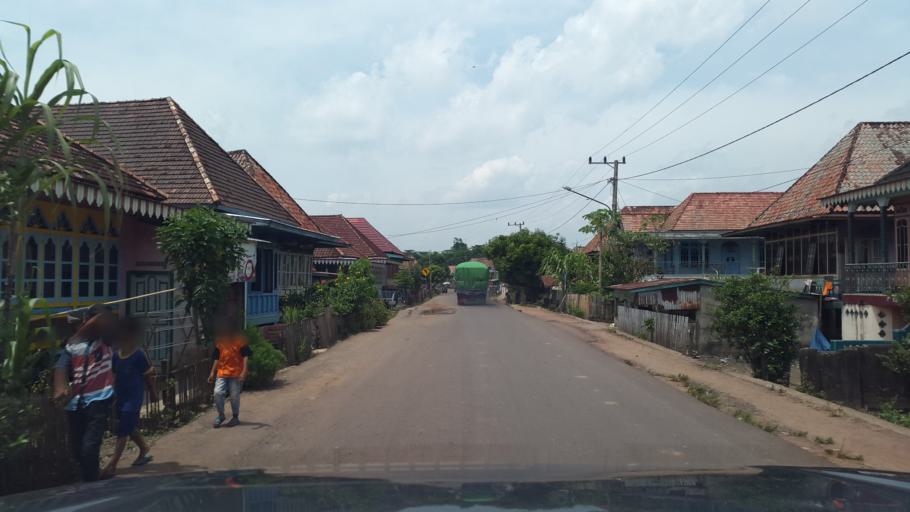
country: ID
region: South Sumatra
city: Tanjung Lubuk
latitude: -3.1729
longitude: 104.8711
